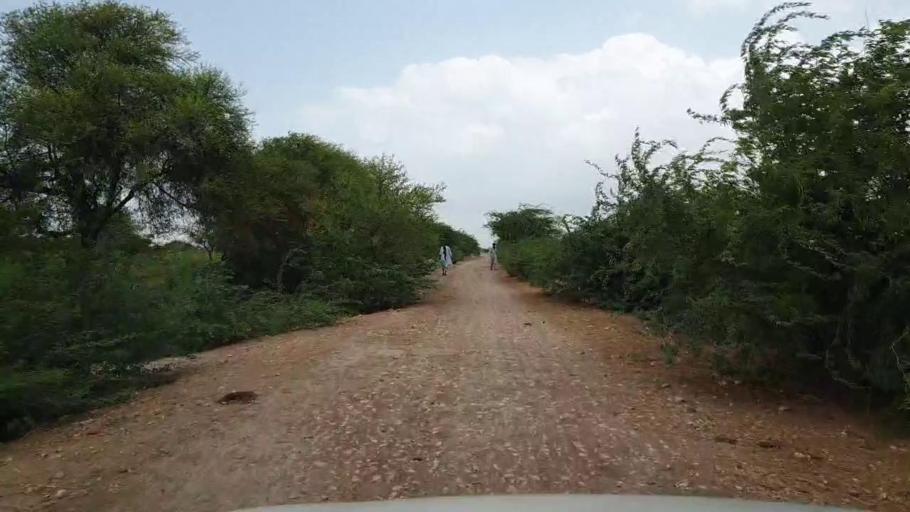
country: PK
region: Sindh
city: Kario
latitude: 24.6915
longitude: 68.6605
